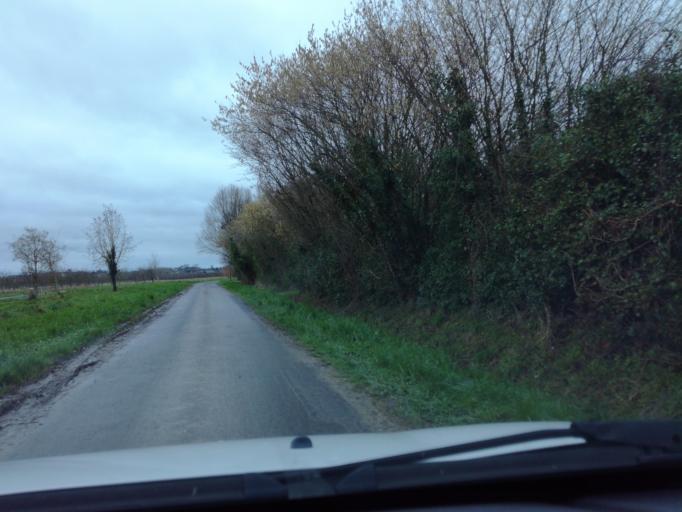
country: FR
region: Brittany
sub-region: Departement d'Ille-et-Vilaine
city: Dol-de-Bretagne
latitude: 48.5623
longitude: -1.7346
